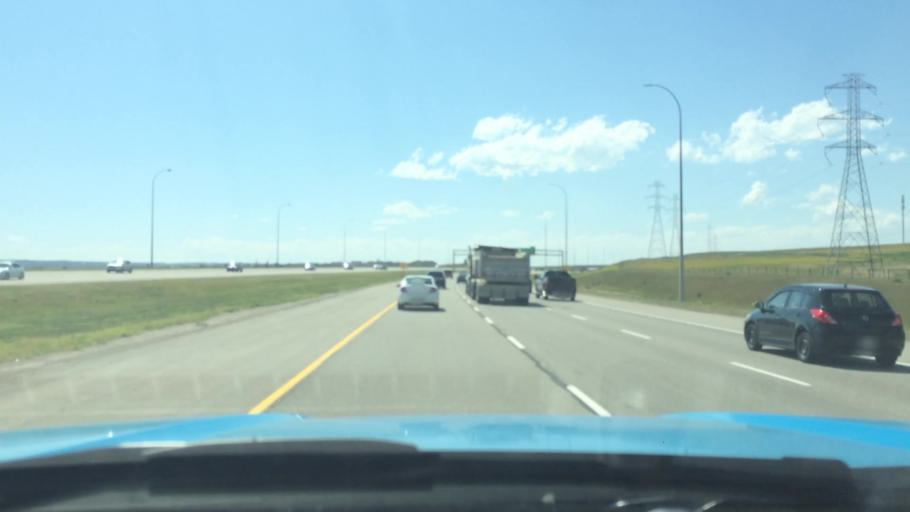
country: CA
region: Alberta
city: Airdrie
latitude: 51.1740
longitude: -114.0545
